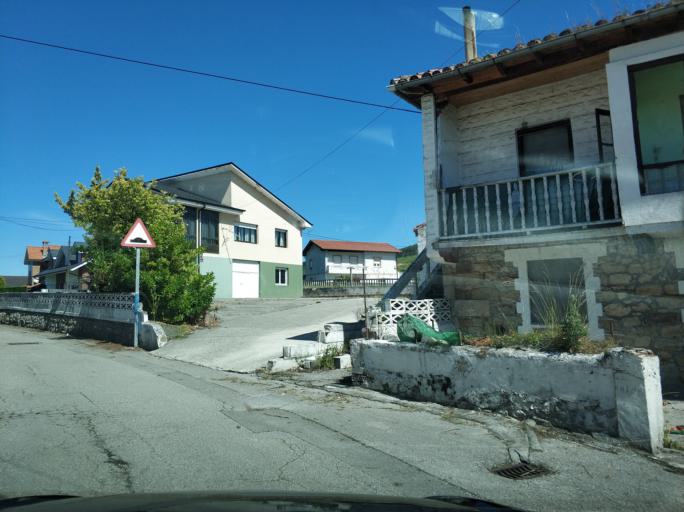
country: ES
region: Cantabria
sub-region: Provincia de Cantabria
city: Puente Viesgo
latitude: 43.3522
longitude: -3.9441
